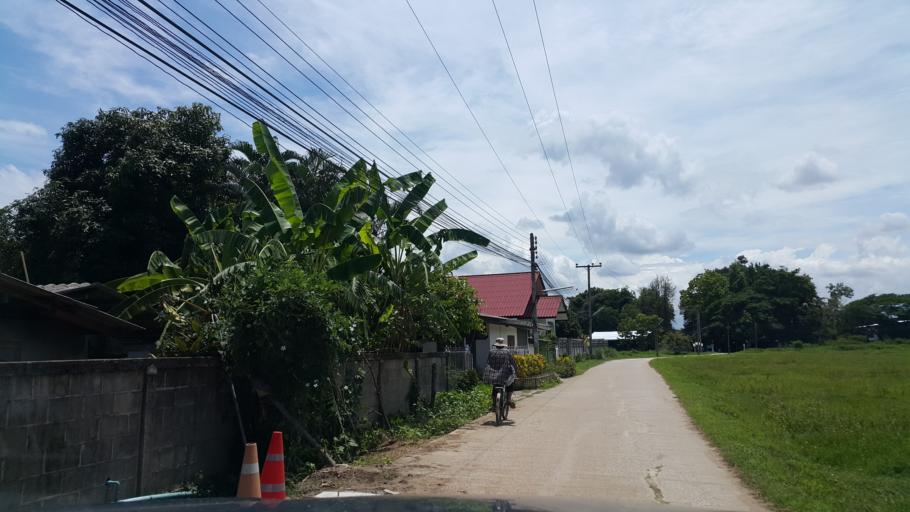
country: TH
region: Chiang Mai
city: Mae On
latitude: 18.7358
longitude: 99.2046
